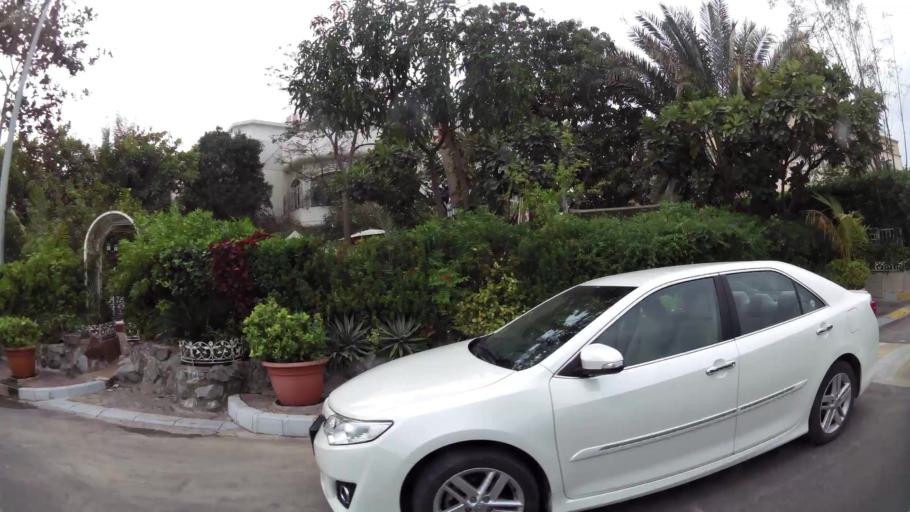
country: AE
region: Abu Dhabi
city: Abu Dhabi
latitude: 24.4317
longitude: 54.4015
